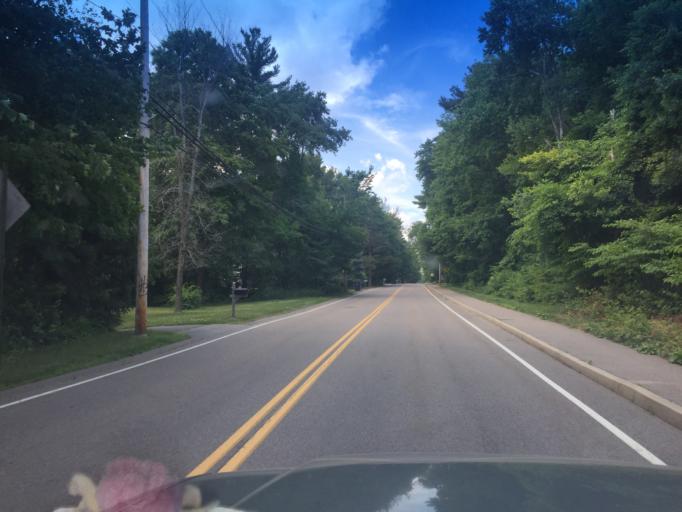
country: US
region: Massachusetts
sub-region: Norfolk County
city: Medway
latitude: 42.1509
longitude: -71.4195
